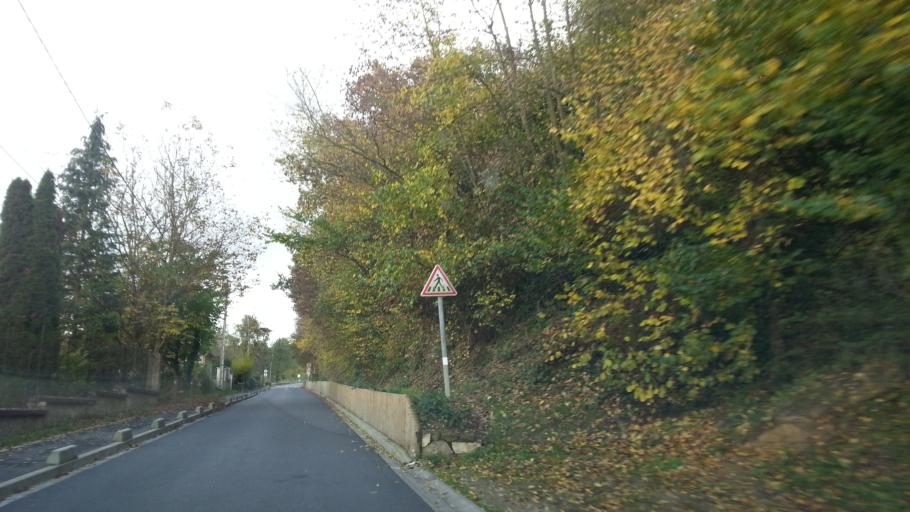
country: FR
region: Picardie
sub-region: Departement de l'Oise
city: Thiverny
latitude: 49.2537
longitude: 2.4028
